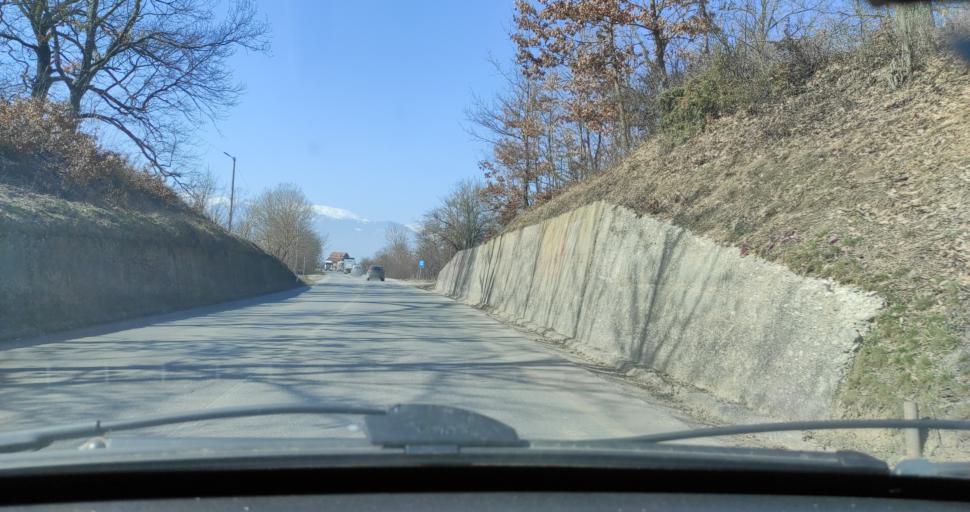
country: XK
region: Pec
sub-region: Komuna e Pejes
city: Kosuriq
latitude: 42.6203
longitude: 20.4838
